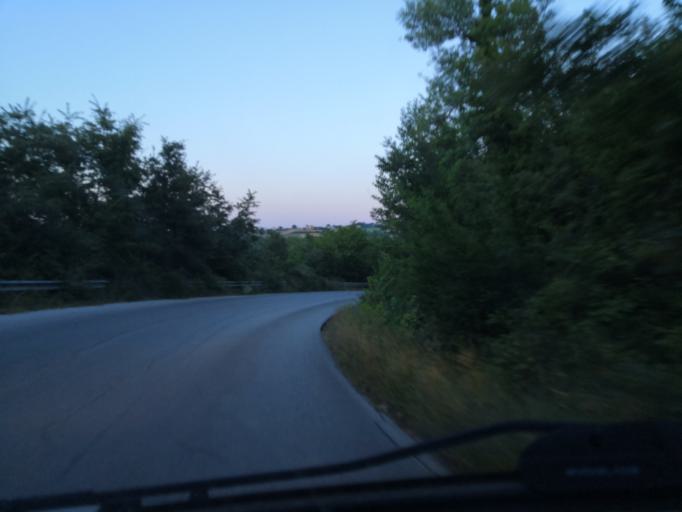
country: IT
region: Molise
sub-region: Provincia di Campobasso
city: Jelsi
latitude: 41.5108
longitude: 14.7814
